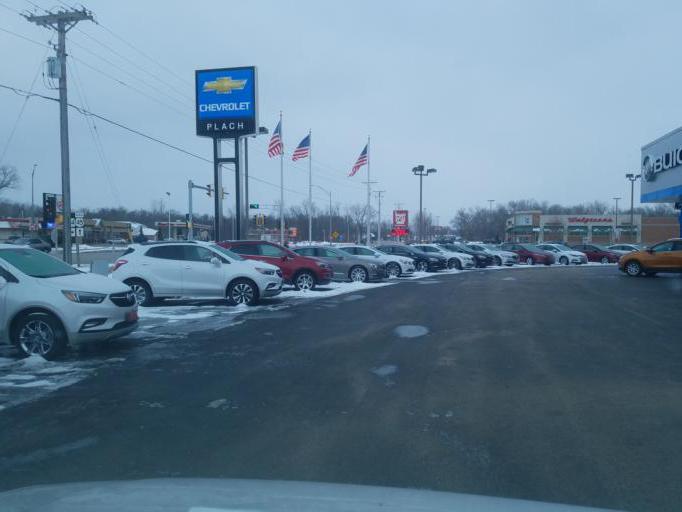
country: US
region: Wisconsin
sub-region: Waupaca County
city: New London
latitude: 44.4033
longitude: -88.7435
